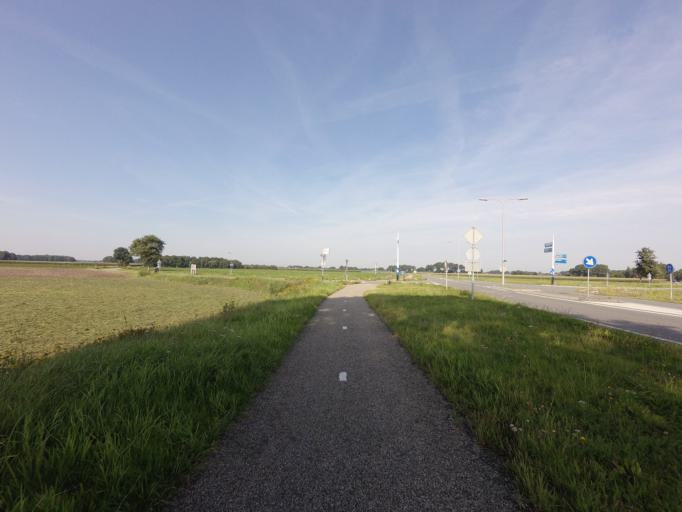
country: DE
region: Lower Saxony
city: Wielen
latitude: 52.5536
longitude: 6.6813
